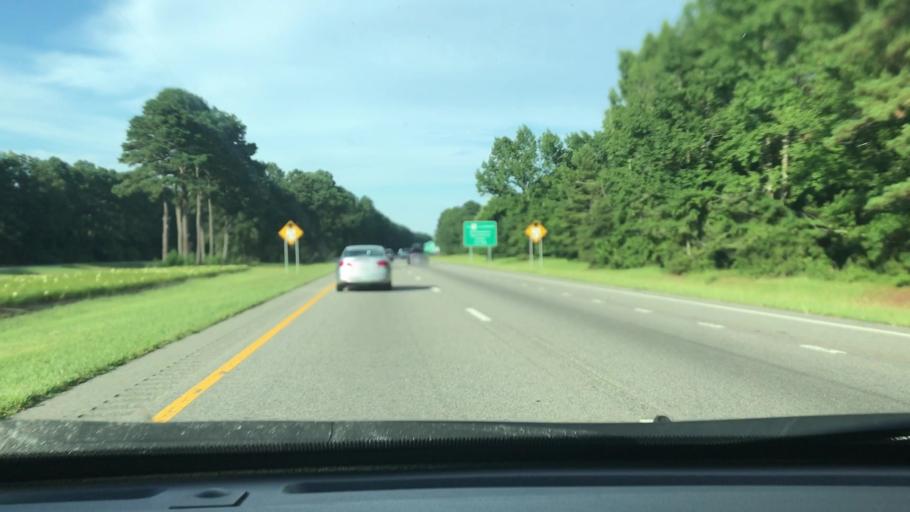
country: US
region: North Carolina
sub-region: Robeson County
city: Fairmont
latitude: 34.5796
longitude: -79.1459
